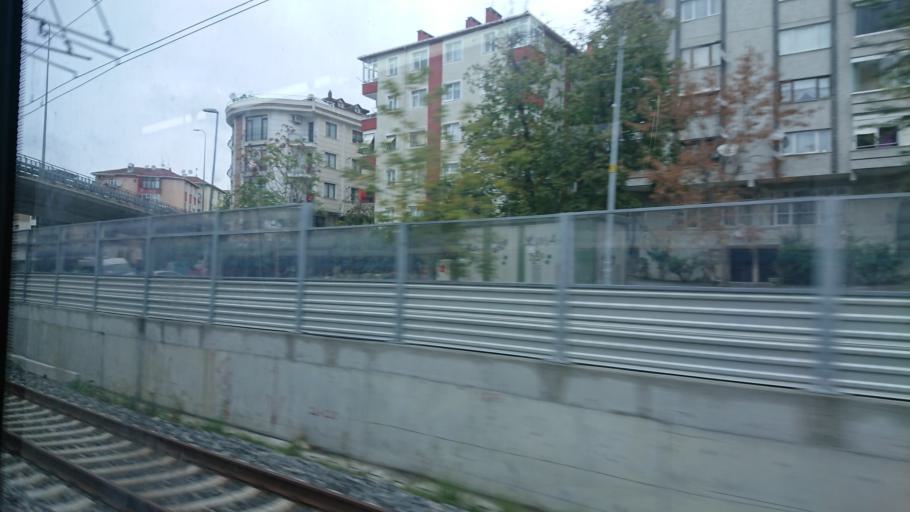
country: TR
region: Istanbul
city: Mahmutbey
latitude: 40.9935
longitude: 28.7696
